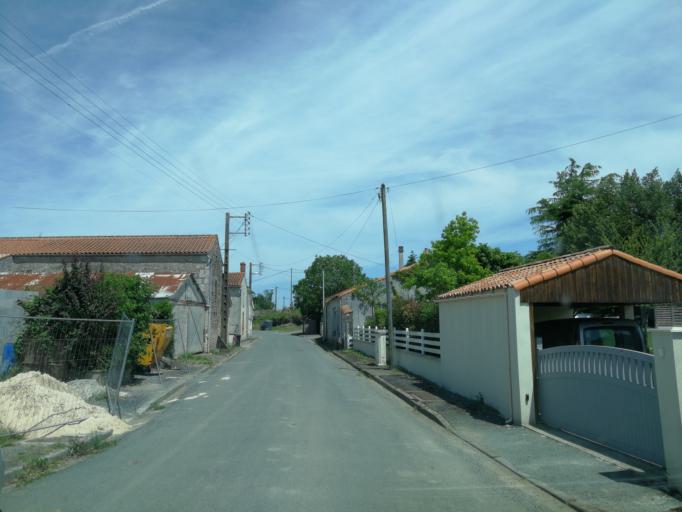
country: FR
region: Pays de la Loire
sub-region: Departement de la Vendee
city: Le Langon
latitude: 46.4176
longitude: -0.9075
